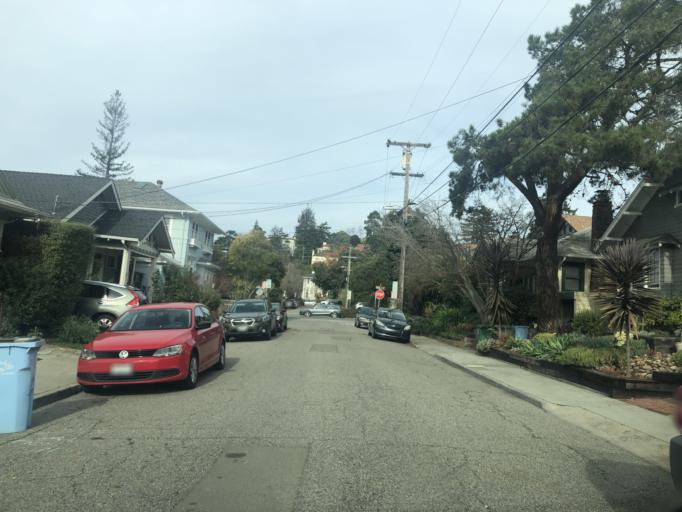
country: US
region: California
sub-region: Alameda County
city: Berkeley
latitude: 37.8574
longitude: -122.2484
